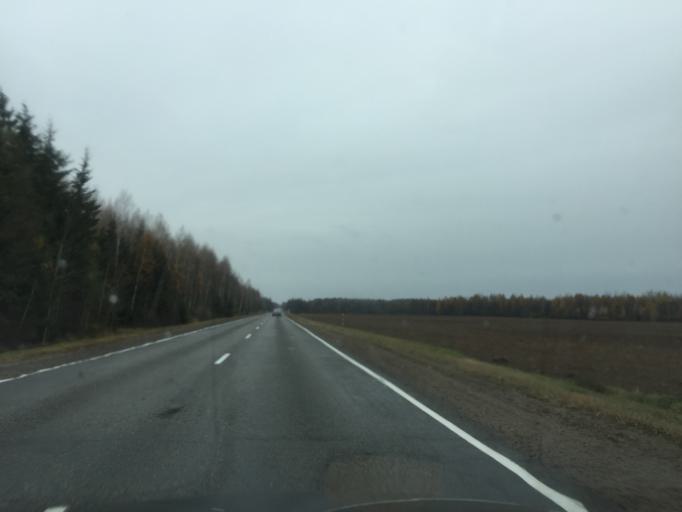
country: BY
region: Mogilev
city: Chavusy
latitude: 53.7133
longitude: 31.1382
